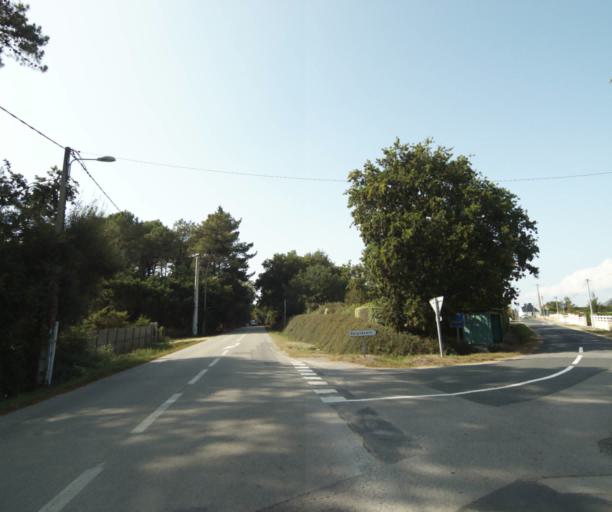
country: FR
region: Brittany
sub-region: Departement du Morbihan
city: Merlevenez
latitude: 47.7049
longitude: -3.2641
